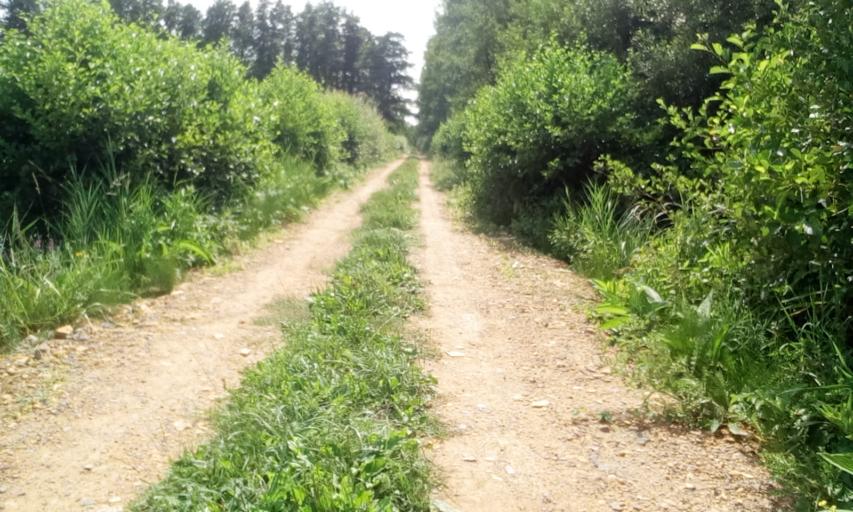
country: FR
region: Lower Normandy
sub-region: Departement du Calvados
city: Bavent
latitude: 49.2370
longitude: -0.1636
